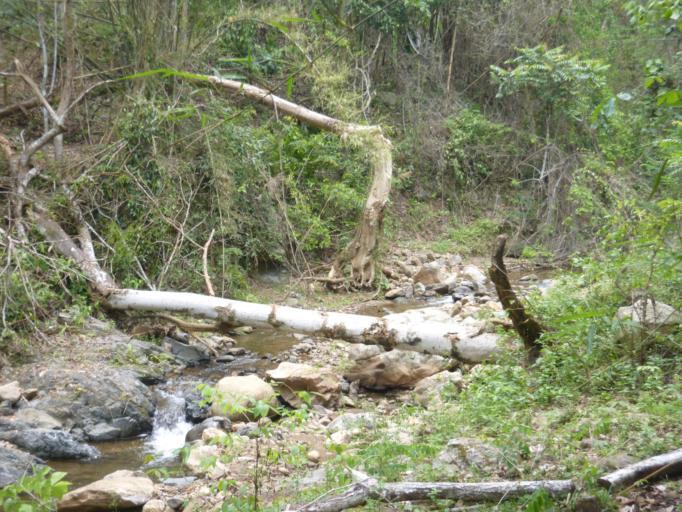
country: TH
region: Chiang Mai
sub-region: Amphoe Chiang Dao
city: Chiang Dao
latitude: 19.4686
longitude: 98.9052
